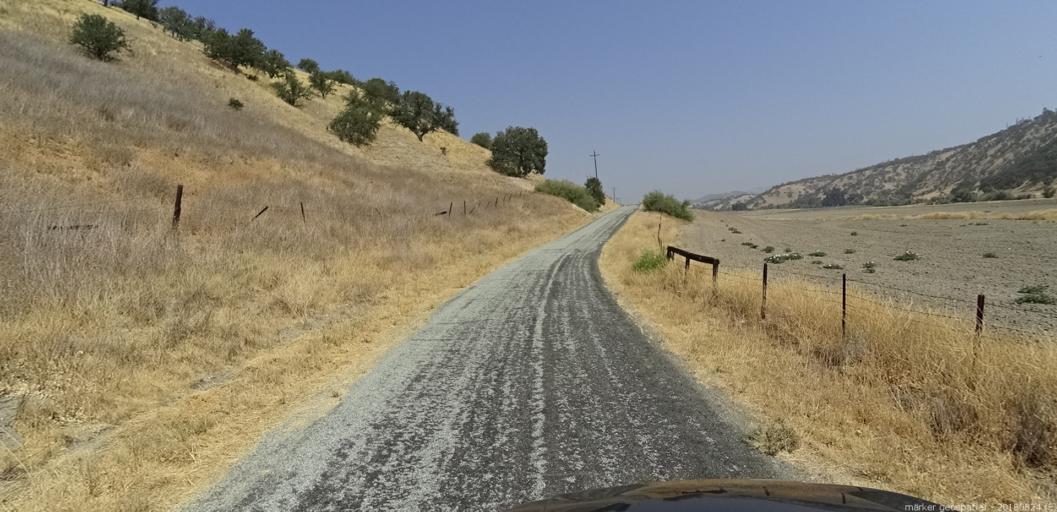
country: US
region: California
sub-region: San Luis Obispo County
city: San Miguel
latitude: 35.9771
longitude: -120.6463
